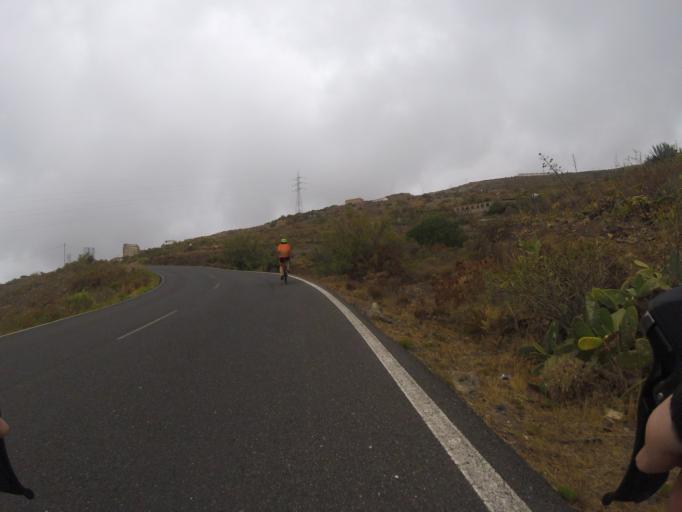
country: ES
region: Canary Islands
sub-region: Provincia de Santa Cruz de Tenerife
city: Guimar
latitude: 28.2926
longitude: -16.4029
